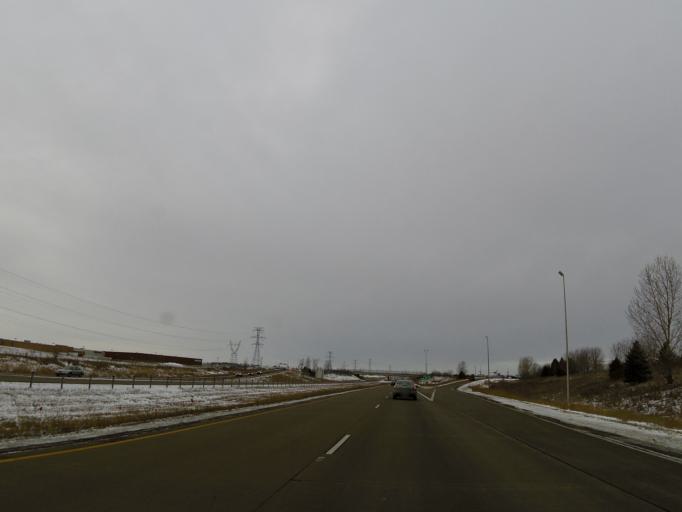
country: US
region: Minnesota
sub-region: Scott County
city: Shakopee
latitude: 44.7788
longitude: -93.4988
